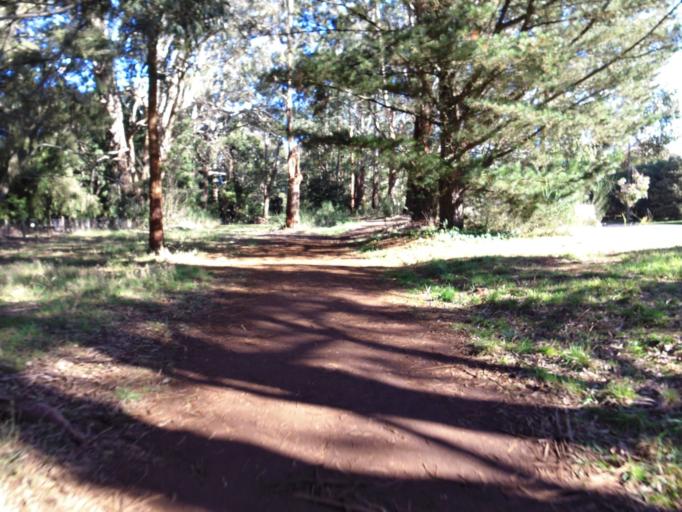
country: AU
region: Victoria
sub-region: Moorabool
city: Bacchus Marsh
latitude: -37.3858
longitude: 144.3152
